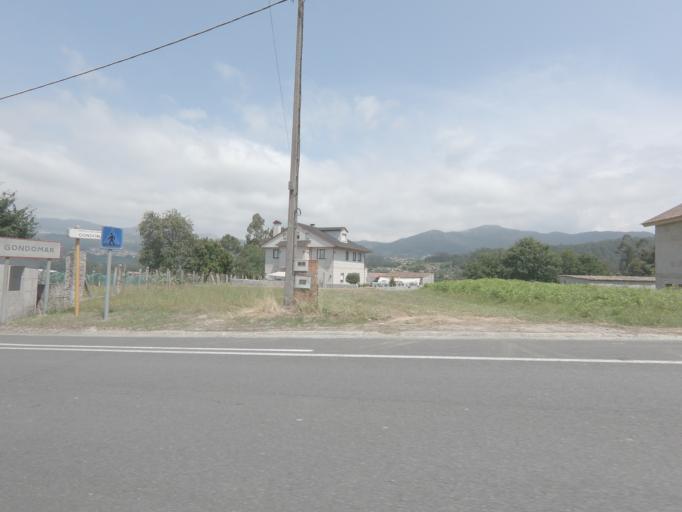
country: ES
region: Galicia
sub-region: Provincia de Pontevedra
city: Gondomar
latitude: 42.0998
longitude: -8.7593
